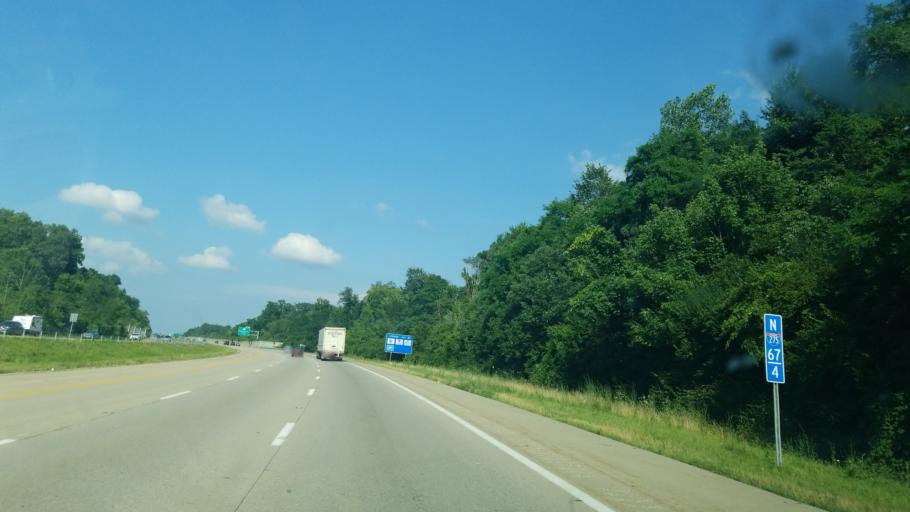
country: US
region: Ohio
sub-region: Hamilton County
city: Cherry Grove
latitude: 39.0572
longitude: -84.3238
